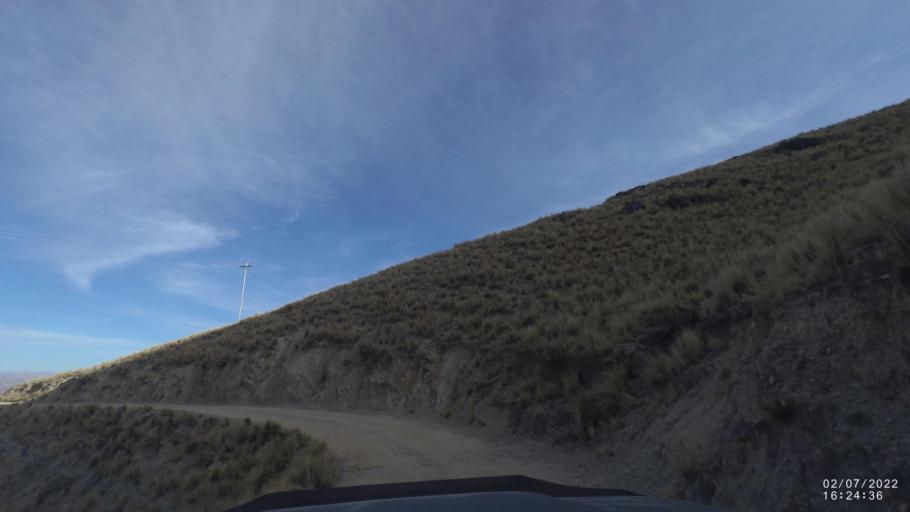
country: BO
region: Cochabamba
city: Irpa Irpa
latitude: -17.9410
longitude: -66.4626
